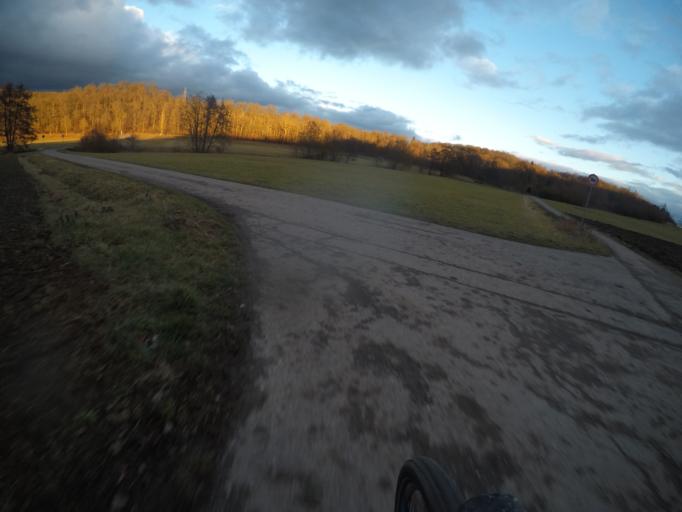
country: DE
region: Baden-Wuerttemberg
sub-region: Regierungsbezirk Stuttgart
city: Ehningen
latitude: 48.6564
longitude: 8.9629
